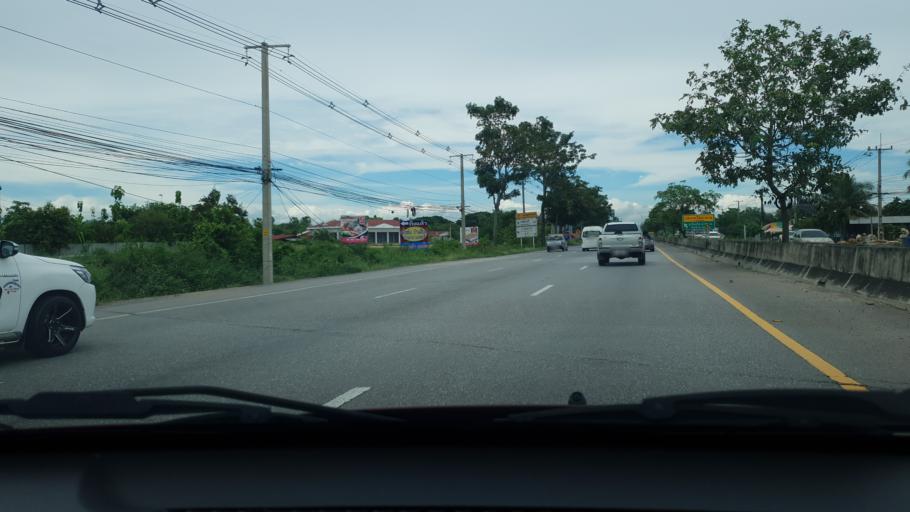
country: TH
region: Phetchaburi
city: Tha Yang
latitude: 12.8718
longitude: 99.9165
